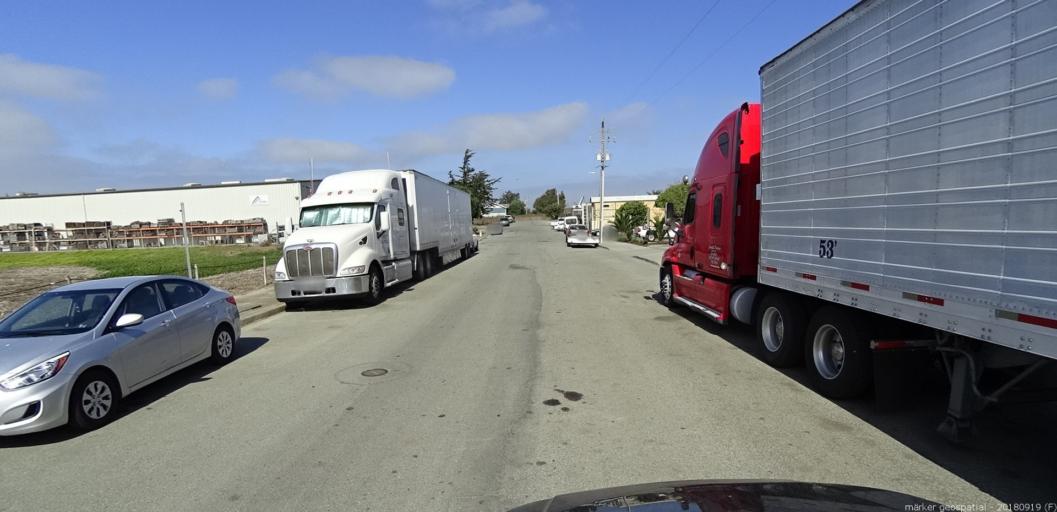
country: US
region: California
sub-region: Monterey County
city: Castroville
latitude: 36.7665
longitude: -121.7601
